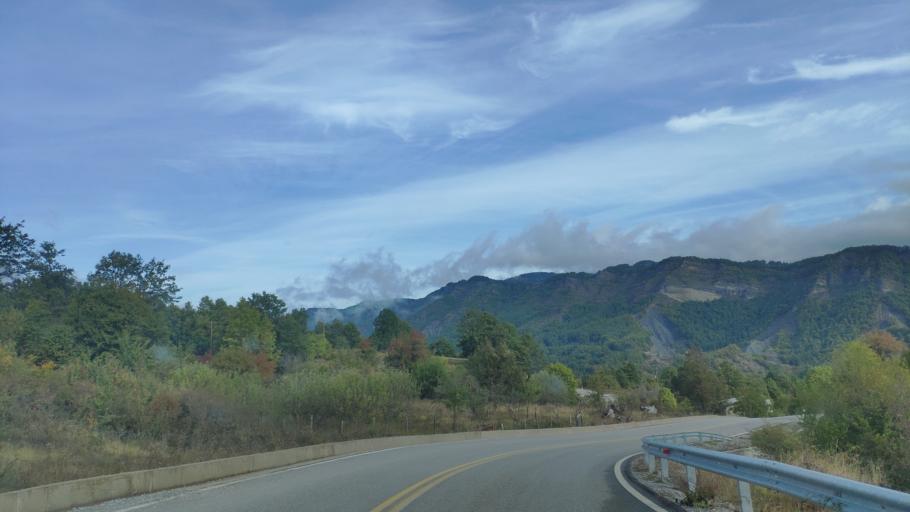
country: GR
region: West Macedonia
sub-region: Nomos Kastorias
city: Nestorio
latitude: 40.2768
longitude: 20.9739
